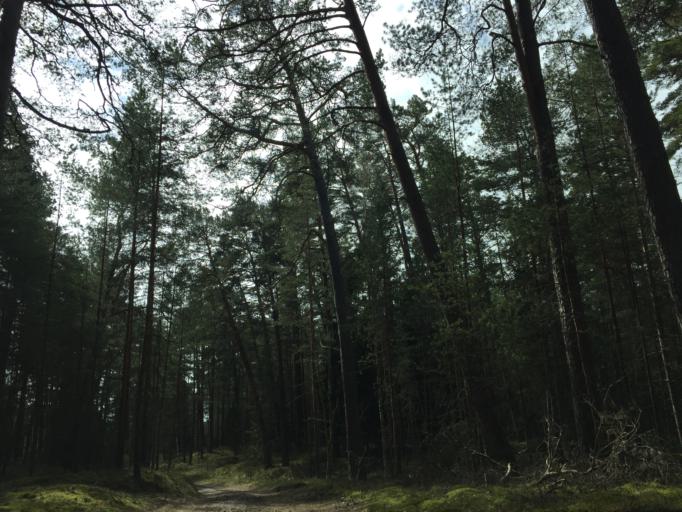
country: LV
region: Salacgrivas
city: Salacgriva
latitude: 57.6893
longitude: 24.3609
